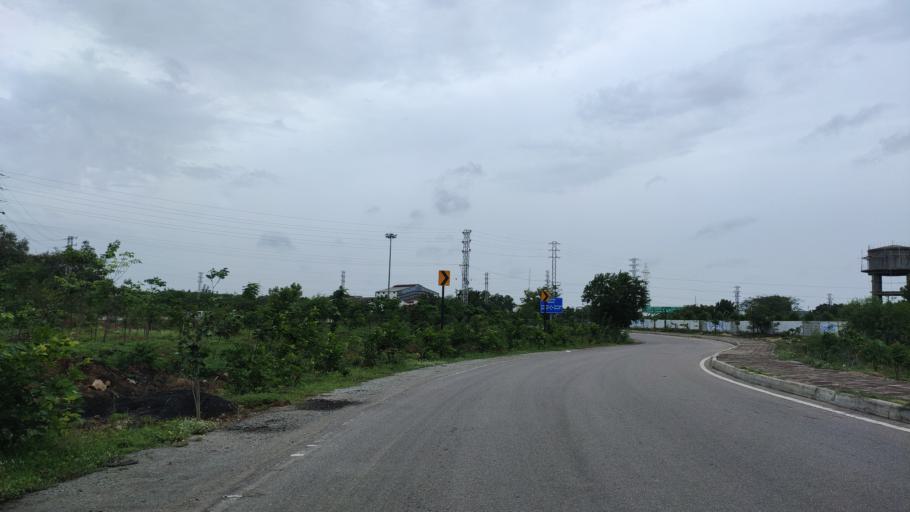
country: IN
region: Telangana
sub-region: Rangareddi
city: Secunderabad
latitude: 17.5786
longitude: 78.5757
